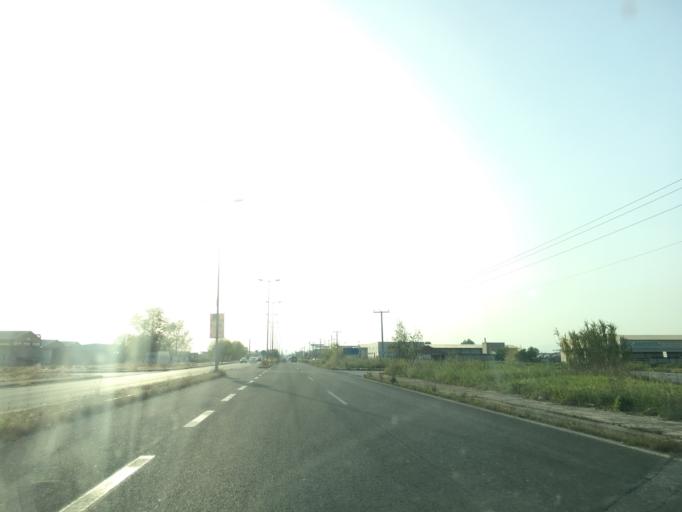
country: GR
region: Thessaly
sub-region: Nomos Larisis
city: Platykampos
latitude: 39.6252
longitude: 22.4829
